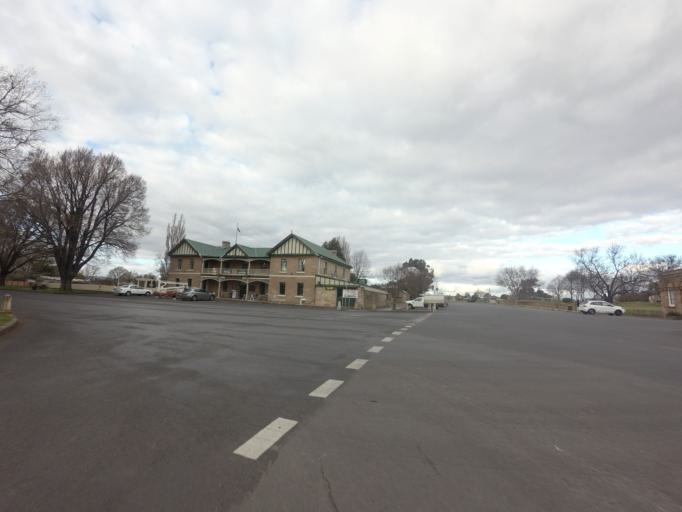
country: AU
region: Tasmania
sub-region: Northern Midlands
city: Evandale
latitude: -42.0309
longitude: 147.4920
